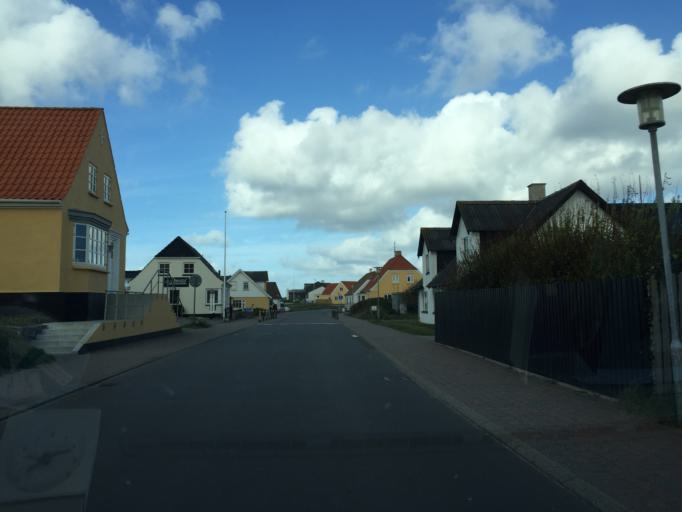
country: DK
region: North Denmark
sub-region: Thisted Kommune
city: Hanstholm
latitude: 57.0416
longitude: 8.4845
